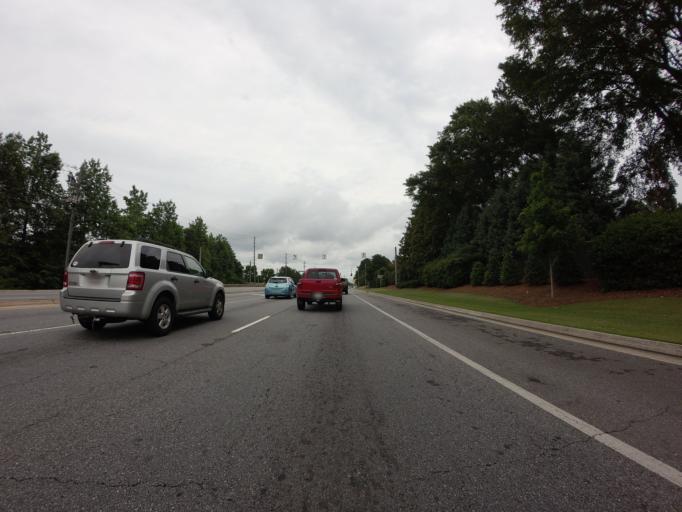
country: US
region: Georgia
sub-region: Fulton County
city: Johns Creek
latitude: 34.0102
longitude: -84.1922
